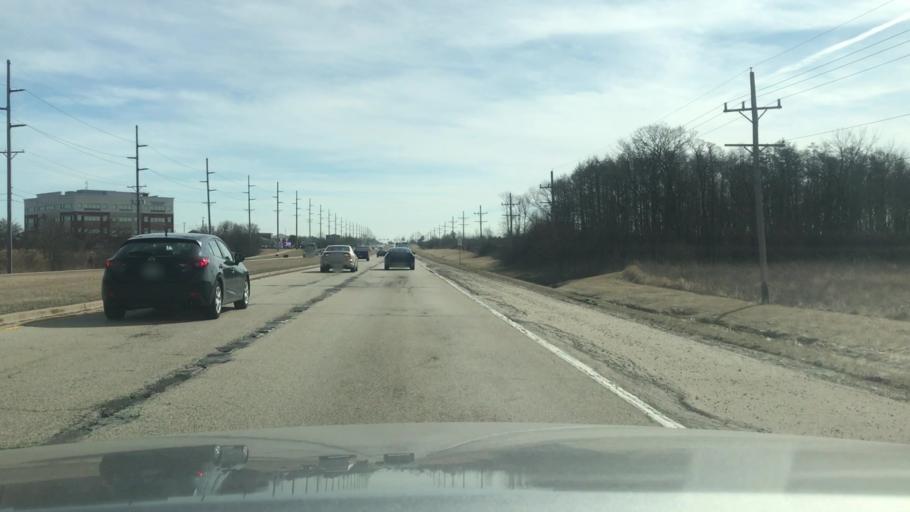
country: US
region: Illinois
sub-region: DuPage County
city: Naperville
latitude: 41.7474
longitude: -88.1793
